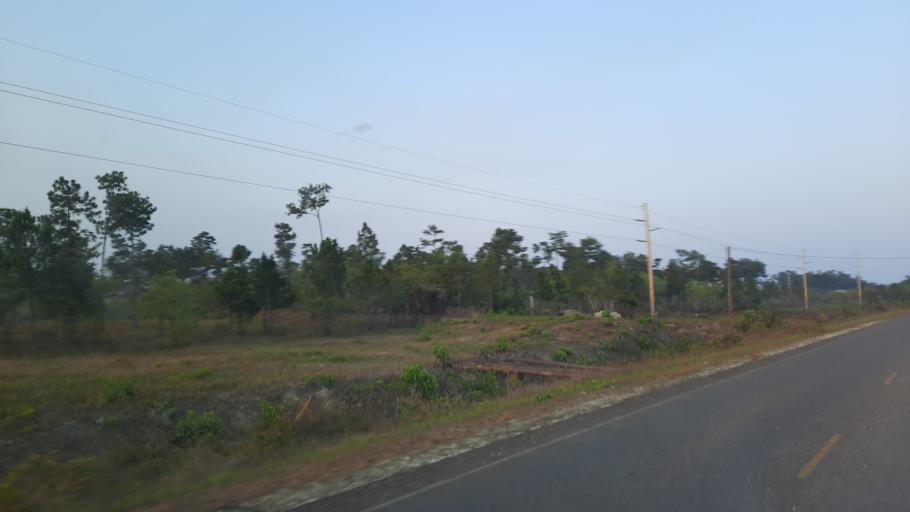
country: BZ
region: Stann Creek
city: Placencia
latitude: 16.5314
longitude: -88.4584
